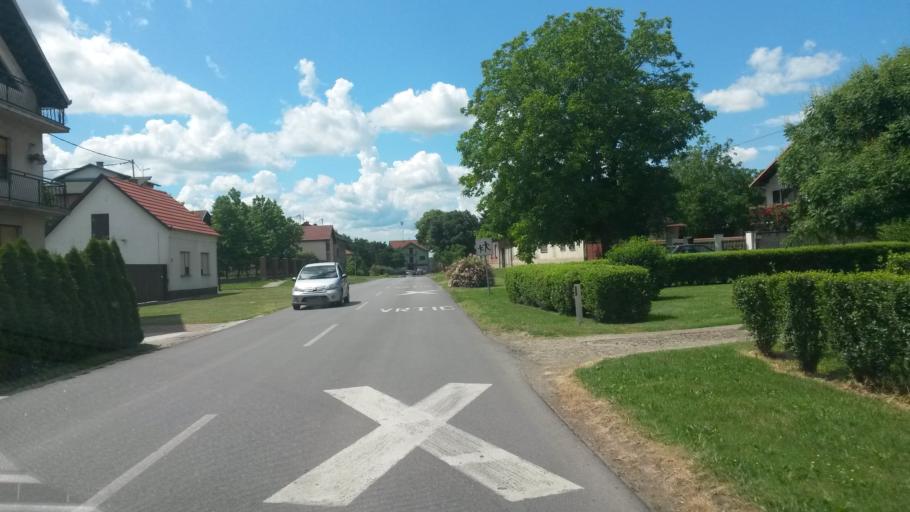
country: HR
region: Osjecko-Baranjska
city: Viskovci
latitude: 45.3158
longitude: 18.4183
